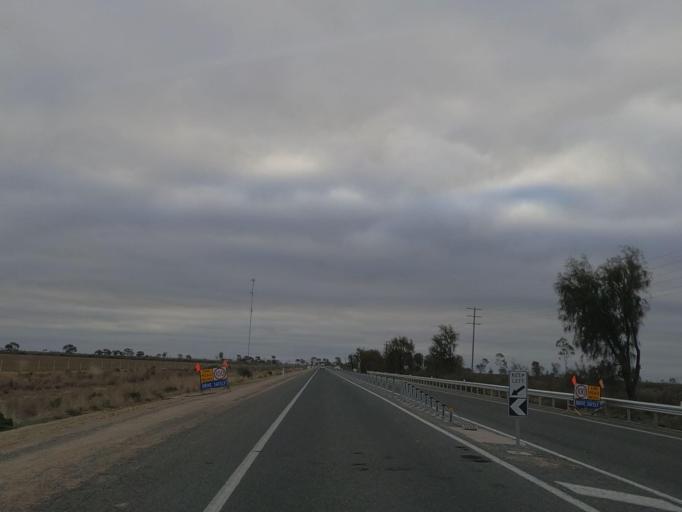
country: AU
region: Victoria
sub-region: Swan Hill
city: Swan Hill
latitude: -35.5318
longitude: 143.7411
